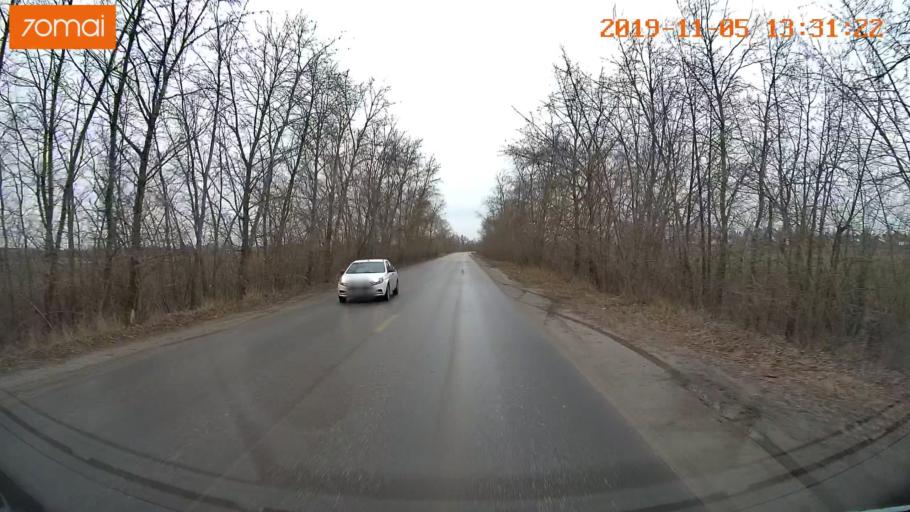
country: RU
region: Ivanovo
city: Shuya
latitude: 56.8751
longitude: 41.3930
